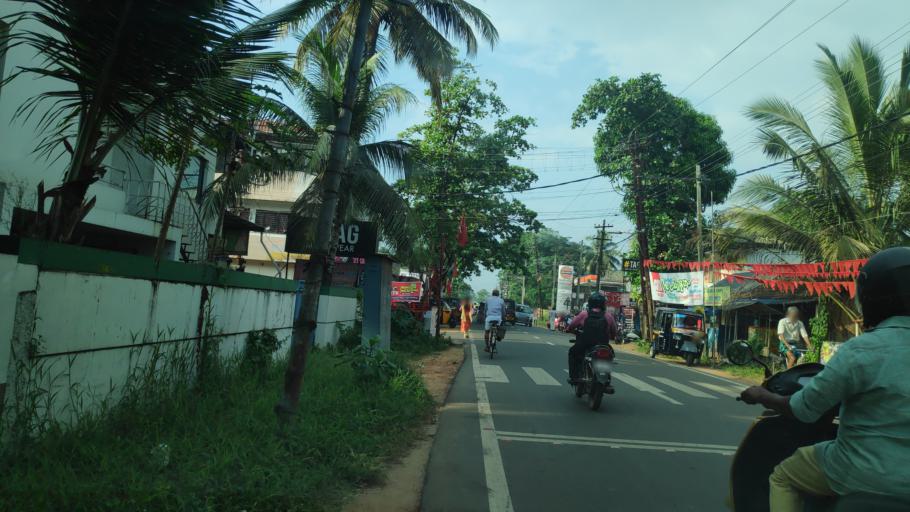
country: IN
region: Kerala
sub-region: Alappuzha
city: Alleppey
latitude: 9.5098
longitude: 76.3391
